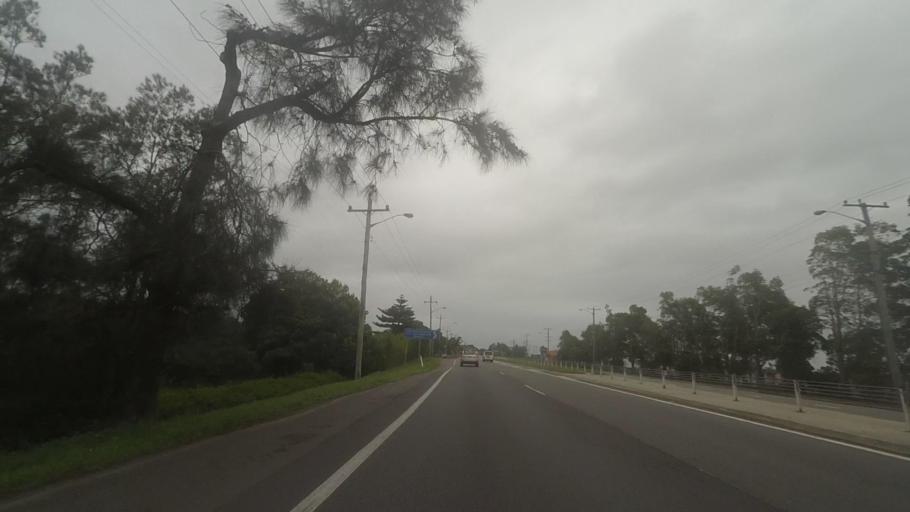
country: AU
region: New South Wales
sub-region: Newcastle
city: Mayfield West
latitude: -32.8680
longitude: 151.7084
